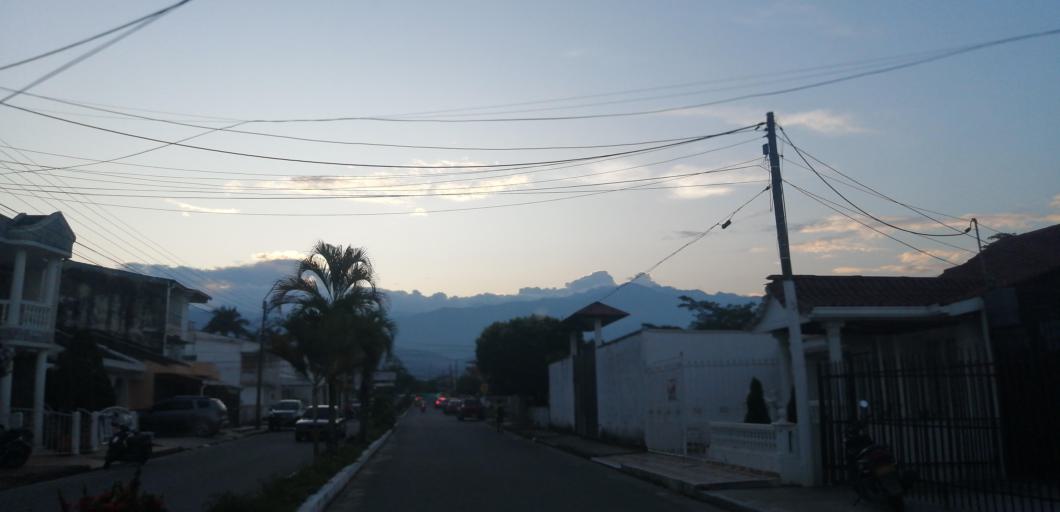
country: CO
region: Meta
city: Acacias
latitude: 3.9931
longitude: -73.7635
